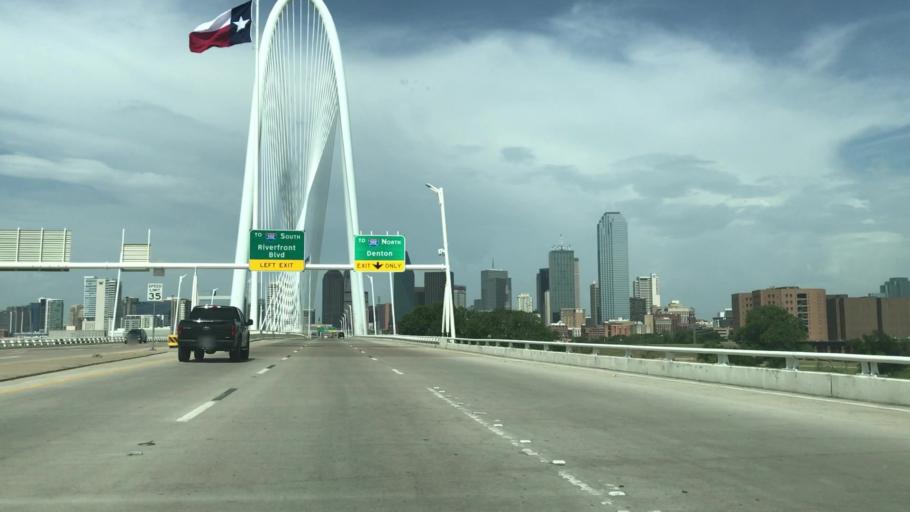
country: US
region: Texas
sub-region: Dallas County
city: Dallas
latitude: 32.7789
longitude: -96.8250
